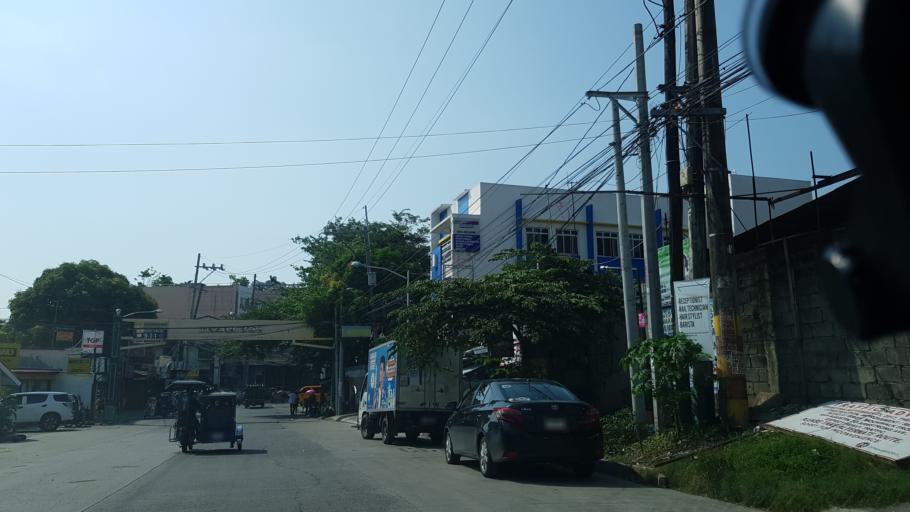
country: PH
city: Sambayanihan People's Village
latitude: 14.4894
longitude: 121.0195
